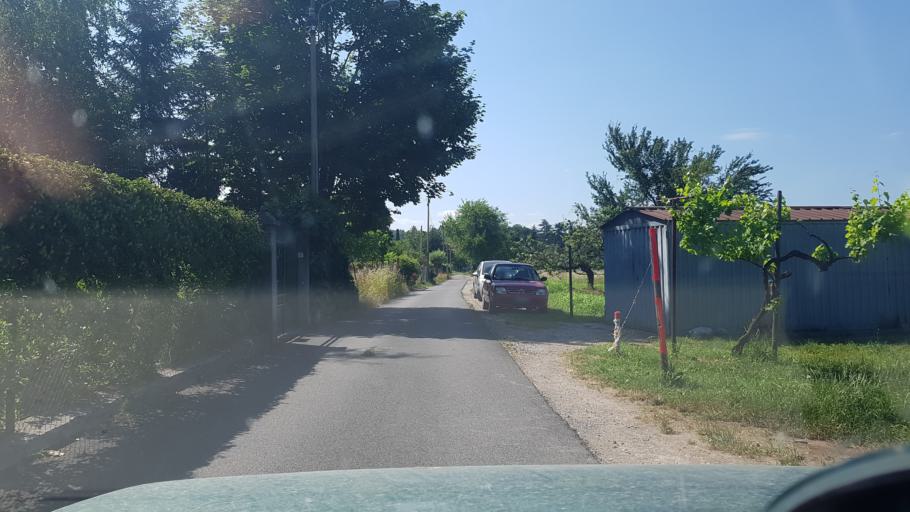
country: SI
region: Nova Gorica
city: Nova Gorica
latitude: 45.9613
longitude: 13.6313
